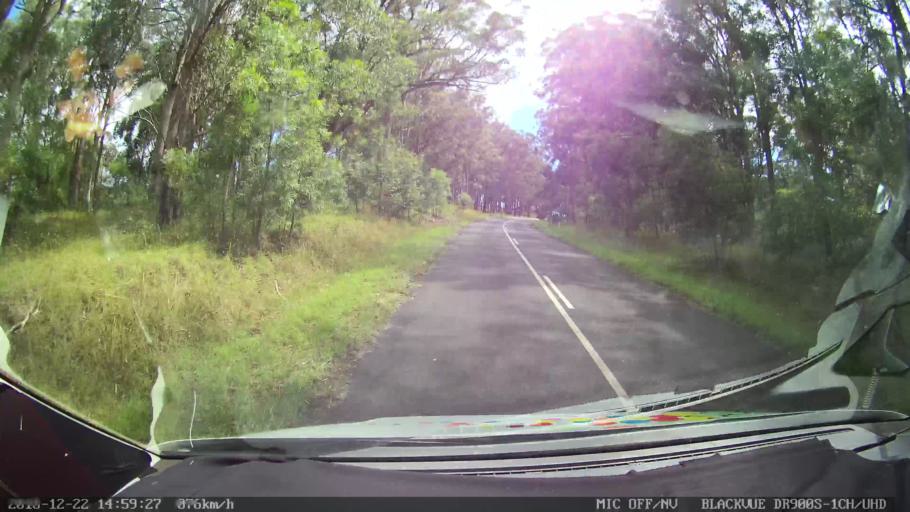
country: AU
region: New South Wales
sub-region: Bellingen
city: Dorrigo
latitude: -30.2470
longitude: 152.4815
